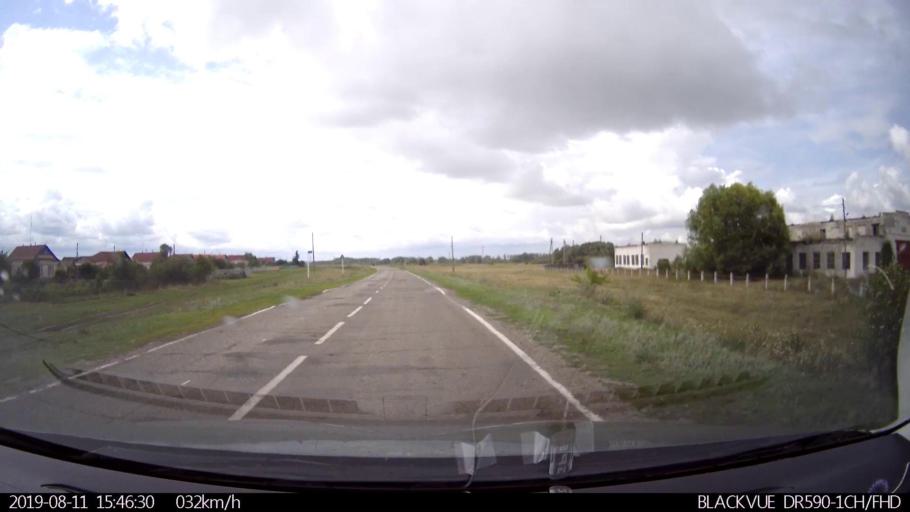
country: RU
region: Ulyanovsk
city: Ignatovka
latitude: 53.8826
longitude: 47.6560
